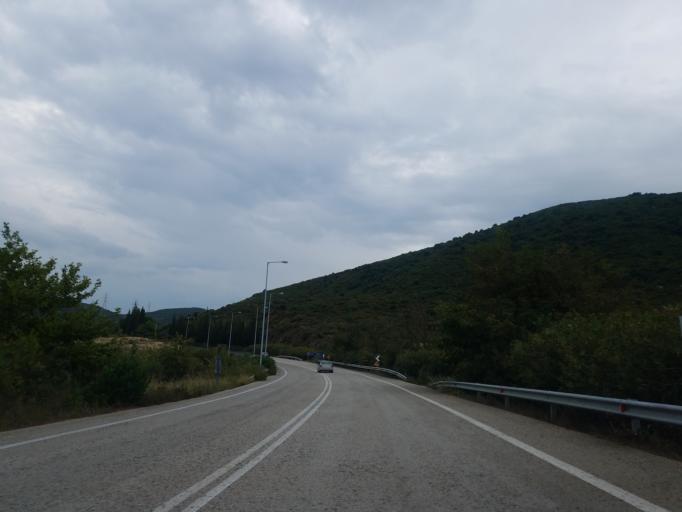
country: GR
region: Central Greece
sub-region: Nomos Voiotias
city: Livadeia
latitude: 38.4478
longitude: 22.7913
